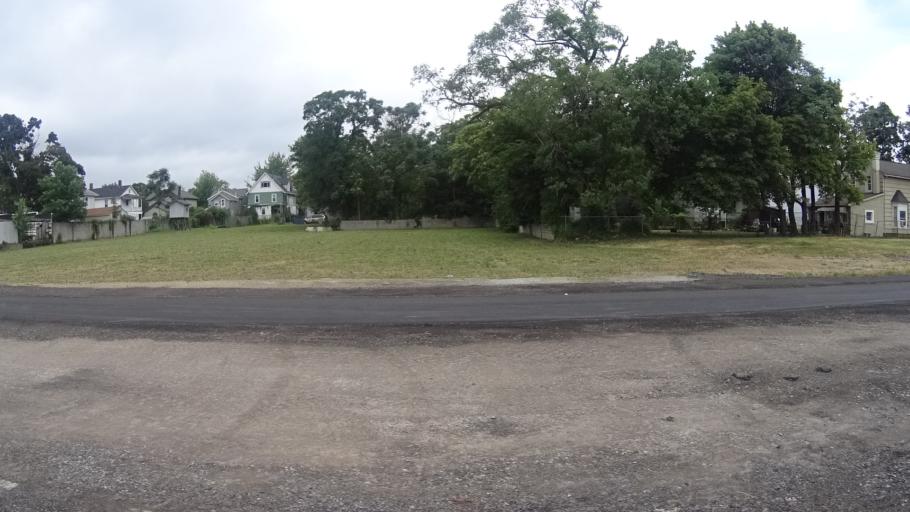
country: US
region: Ohio
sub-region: Erie County
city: Sandusky
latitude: 41.4553
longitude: -82.7036
